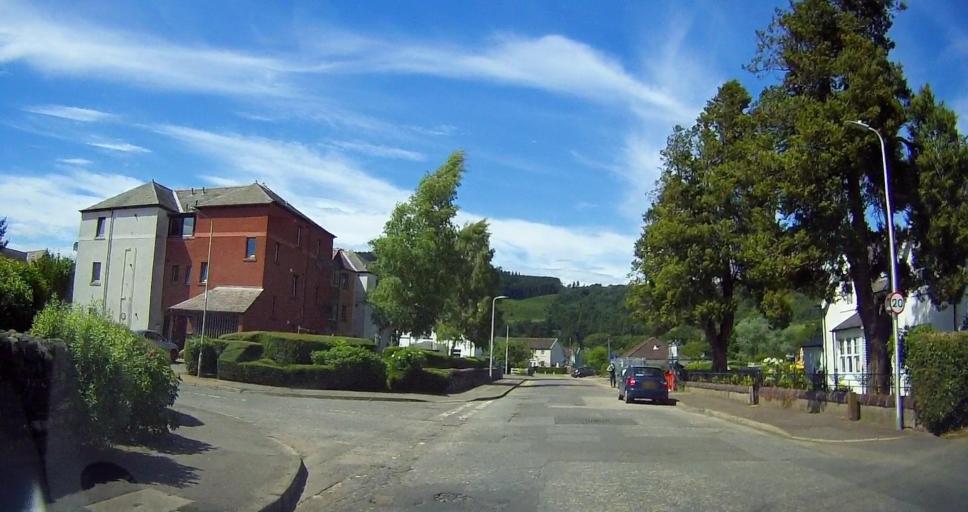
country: GB
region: Scotland
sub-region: Perth and Kinross
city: Aberfeldy
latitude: 56.6224
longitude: -3.8625
